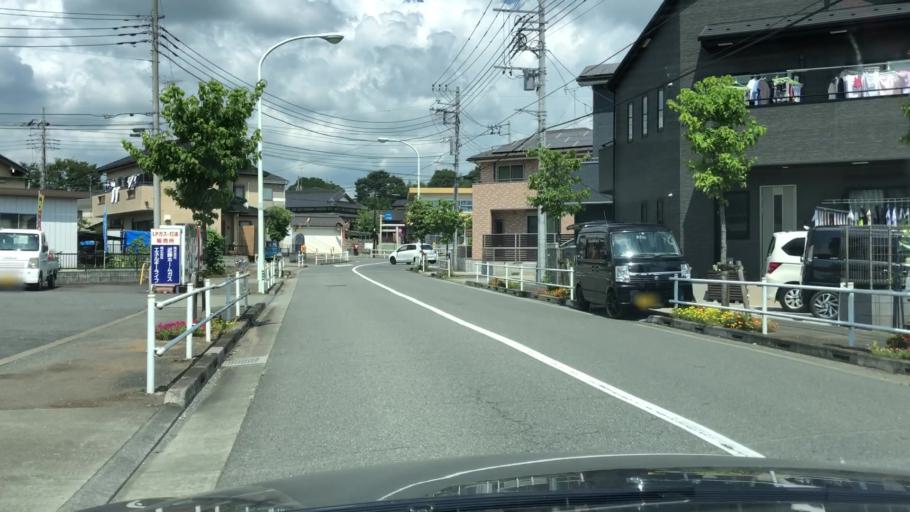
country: JP
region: Tokyo
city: Fussa
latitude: 35.7200
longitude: 139.2787
